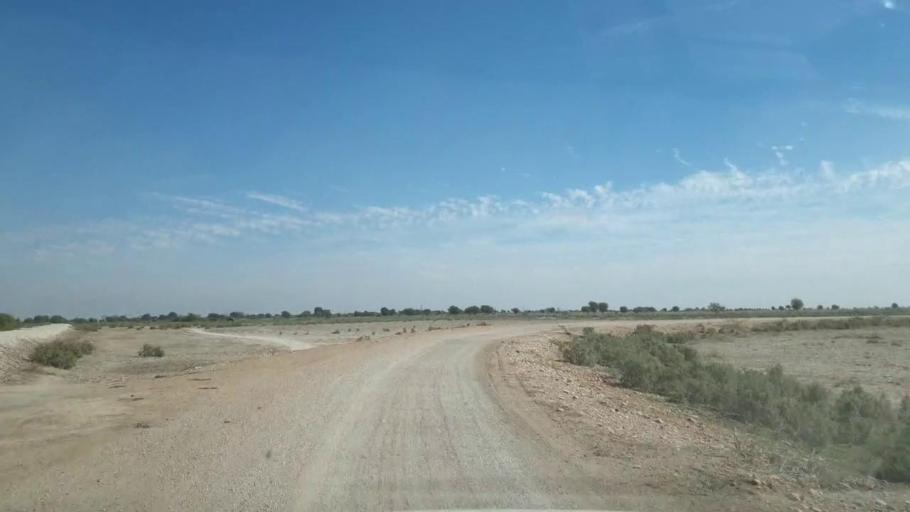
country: PK
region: Sindh
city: Pithoro
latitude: 25.5766
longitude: 69.3046
